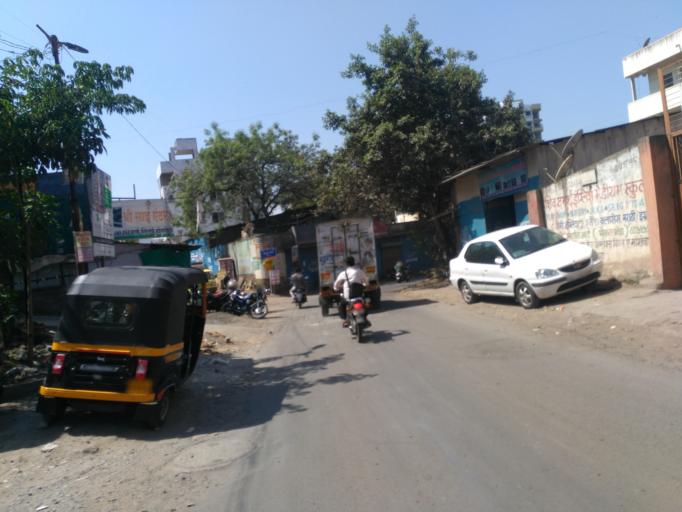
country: IN
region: Maharashtra
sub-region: Pune Division
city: Pune
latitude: 18.4388
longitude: 73.8629
